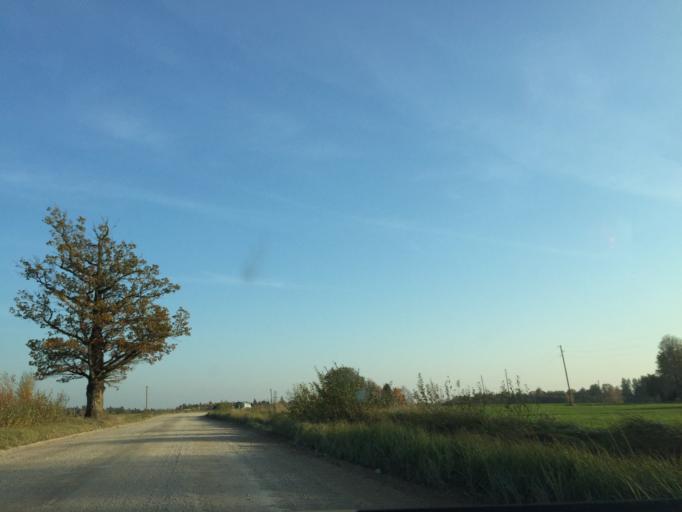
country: LV
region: Vainode
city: Vainode
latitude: 56.6099
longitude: 21.8207
